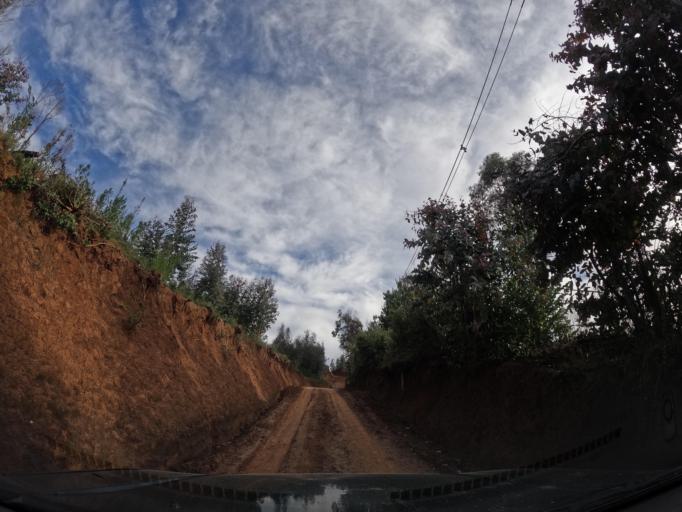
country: CL
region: Biobio
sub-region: Provincia de Concepcion
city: Chiguayante
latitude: -37.0354
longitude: -72.9050
